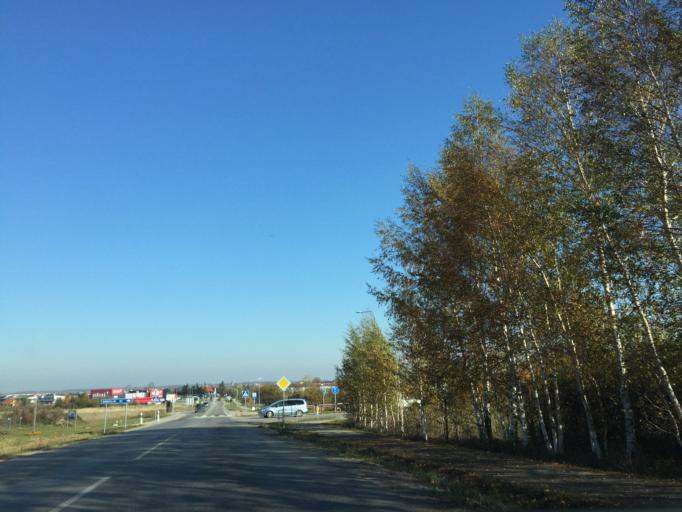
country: LT
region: Klaipedos apskritis
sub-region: Klaipeda
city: Klaipeda
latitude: 55.7331
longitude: 21.1882
